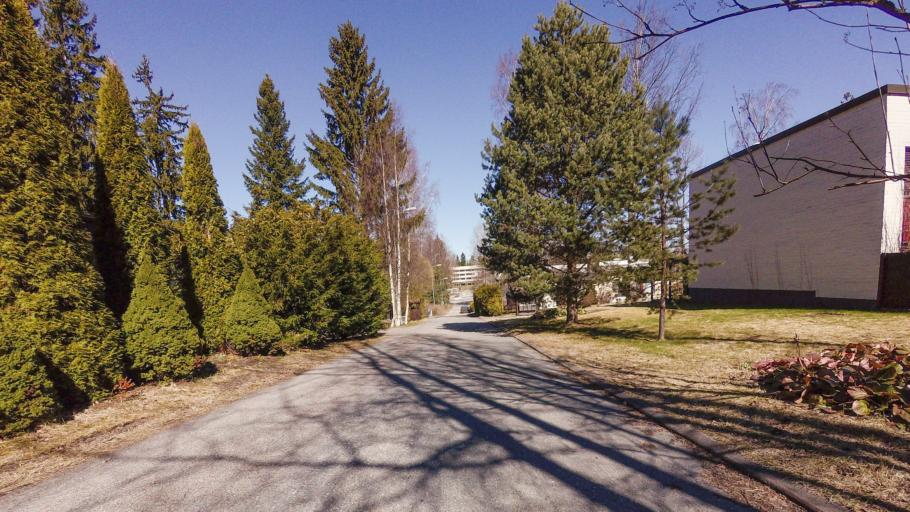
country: FI
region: Uusimaa
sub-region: Helsinki
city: Helsinki
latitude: 60.1739
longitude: 25.0464
